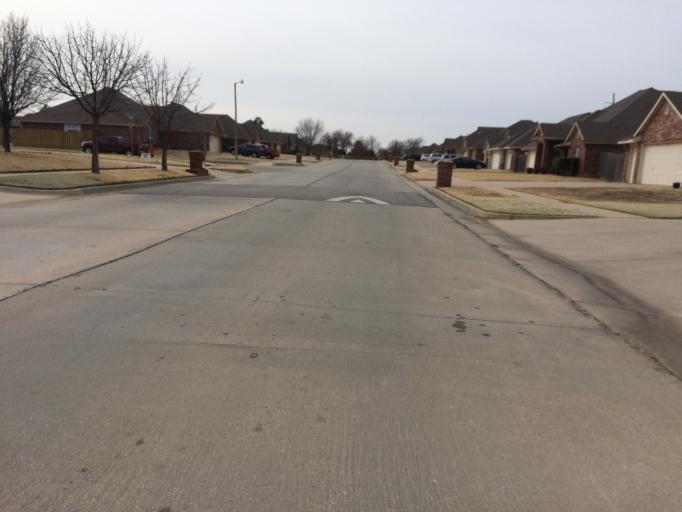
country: US
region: Oklahoma
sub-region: Cleveland County
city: Hall Park
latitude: 35.2173
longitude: -97.3965
